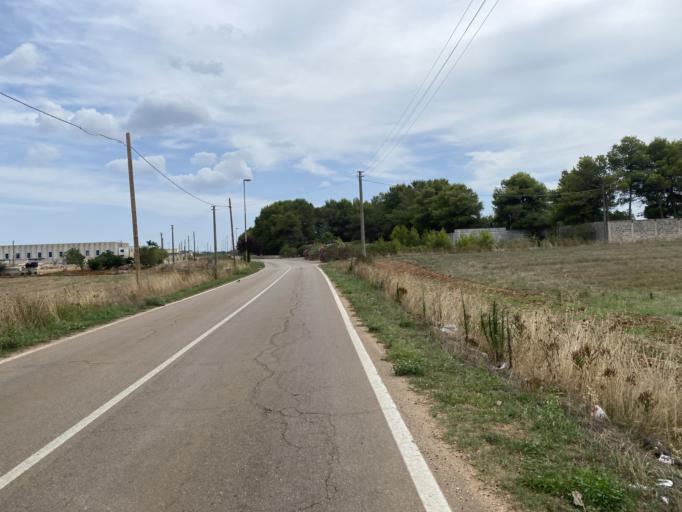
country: IT
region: Apulia
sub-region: Provincia di Lecce
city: Giuggianello
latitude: 40.0880
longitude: 18.3704
